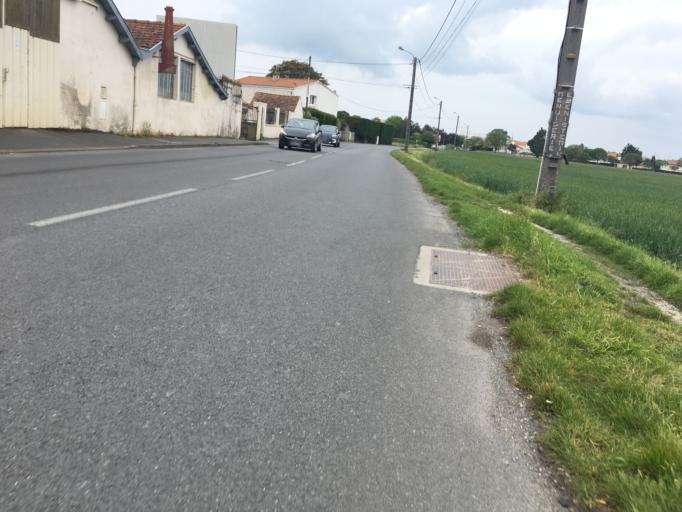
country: FR
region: Poitou-Charentes
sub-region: Departement de la Charente-Maritime
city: Aytre
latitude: 46.1415
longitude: -1.1236
